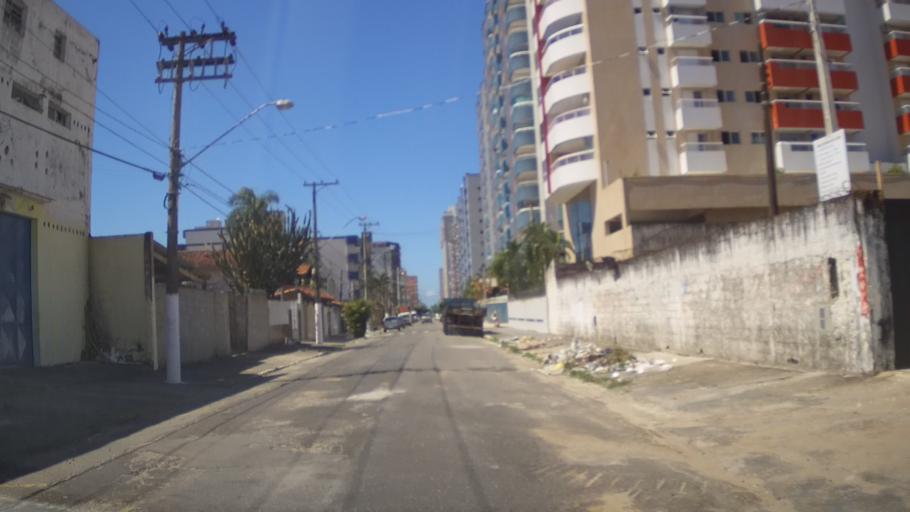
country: BR
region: Sao Paulo
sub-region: Praia Grande
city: Praia Grande
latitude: -24.0239
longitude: -46.4733
